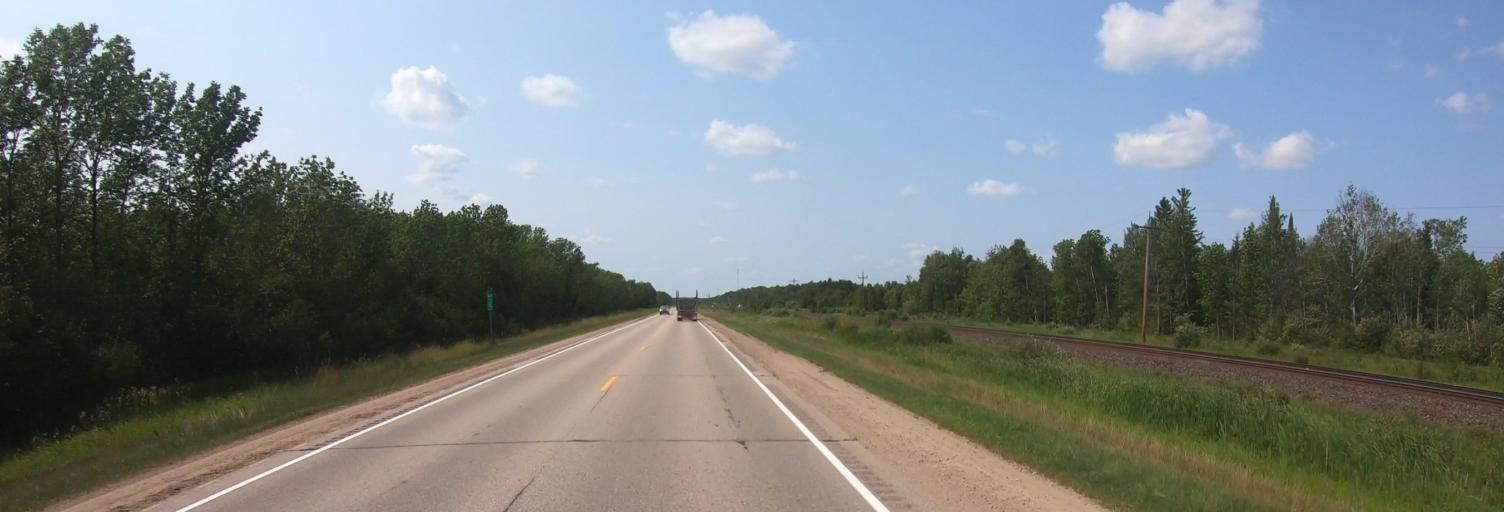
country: US
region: Minnesota
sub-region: Roseau County
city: Warroad
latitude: 48.7919
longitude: -95.0611
